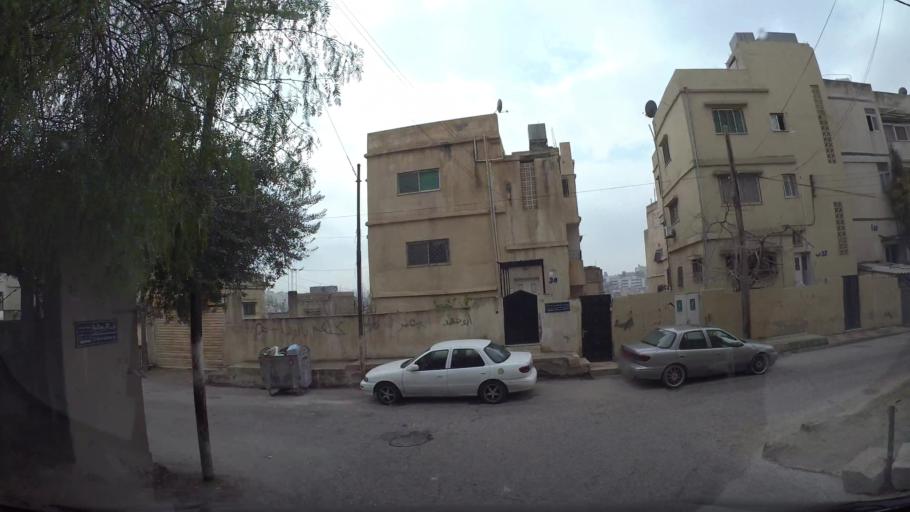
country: JO
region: Amman
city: Amman
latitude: 31.9669
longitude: 35.9320
